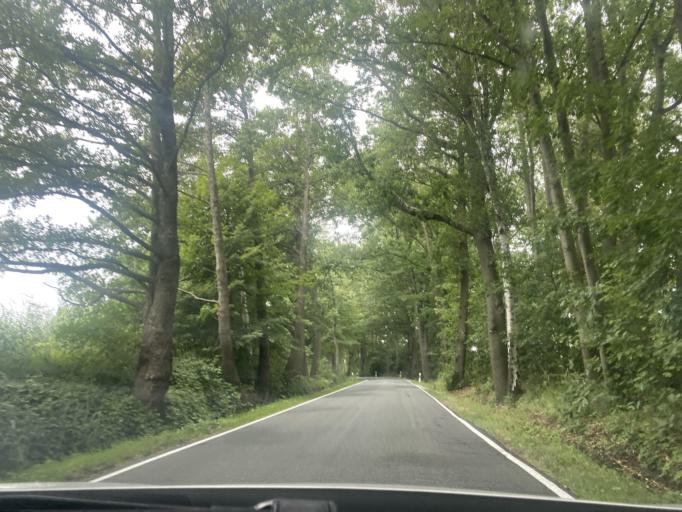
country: DE
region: Saxony
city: Konigswartha
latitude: 51.3247
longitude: 14.3064
